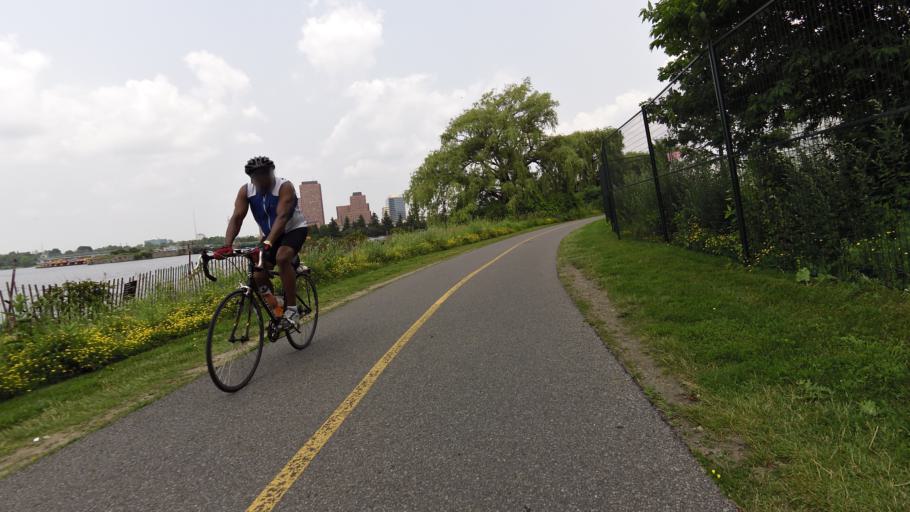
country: CA
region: Ontario
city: Ottawa
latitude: 45.4165
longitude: -75.7201
